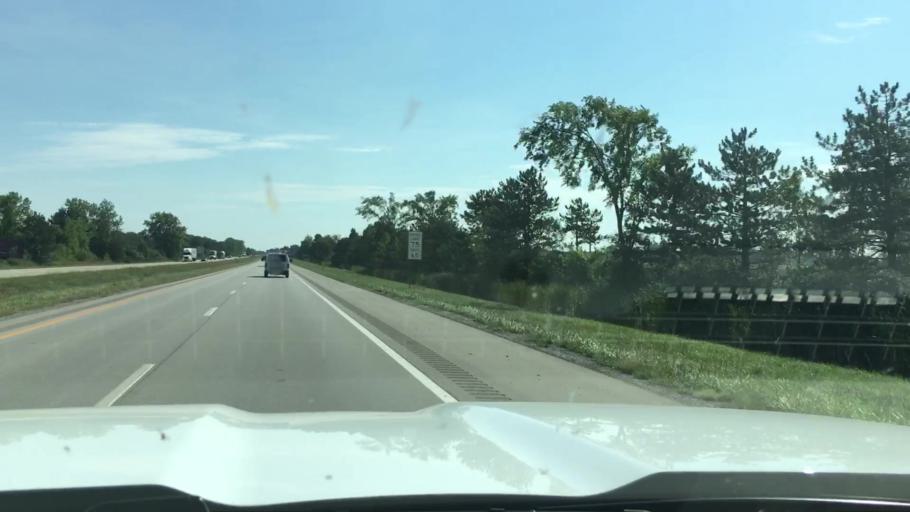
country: US
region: Michigan
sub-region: Bay County
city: Auburn
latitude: 43.5968
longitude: -84.1261
